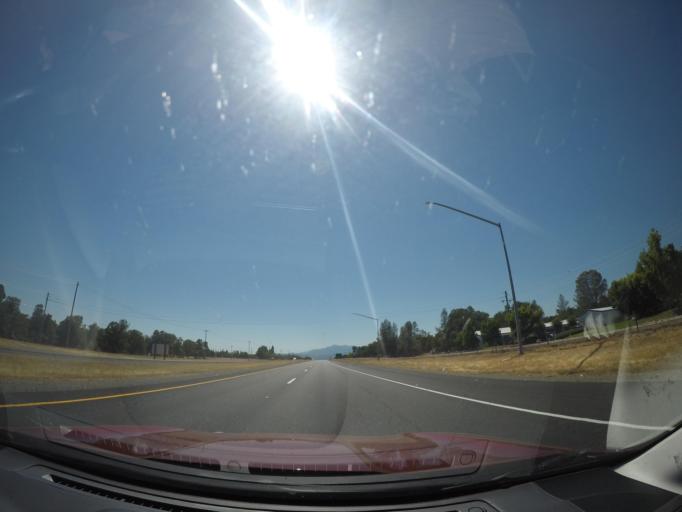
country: US
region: California
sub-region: Shasta County
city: Redding
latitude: 40.6196
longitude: -122.3250
